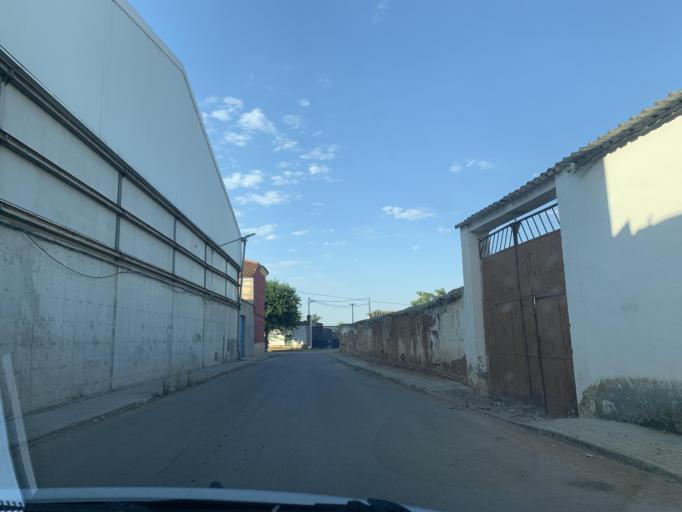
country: ES
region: Castille-La Mancha
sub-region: Provincia de Ciudad Real
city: Argamasilla de Alba
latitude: 39.1690
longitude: -3.2301
